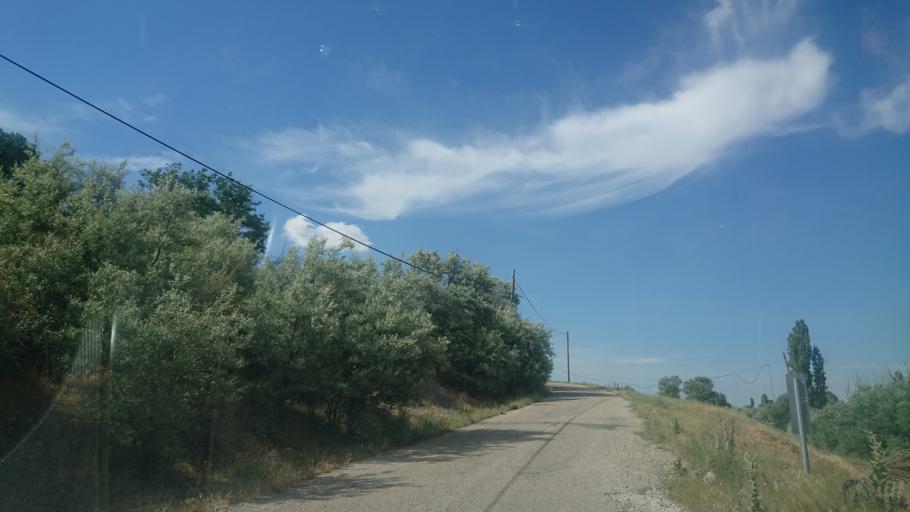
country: TR
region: Aksaray
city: Ortakoy
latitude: 38.8091
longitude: 33.9860
